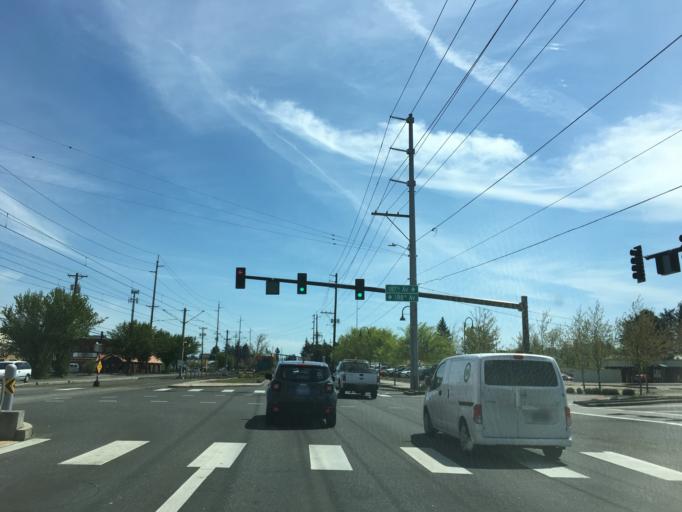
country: US
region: Oregon
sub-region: Multnomah County
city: Fairview
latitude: 45.5204
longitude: -122.4707
